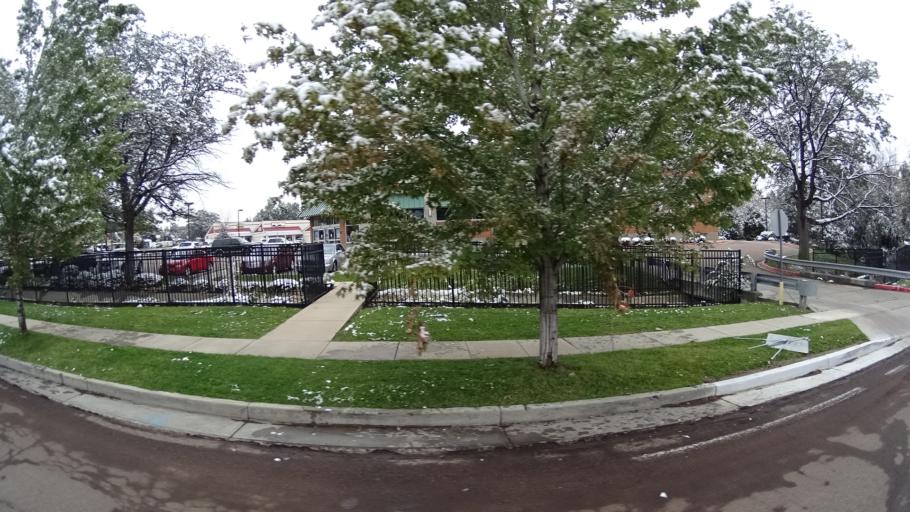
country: US
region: Colorado
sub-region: El Paso County
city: Cimarron Hills
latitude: 38.9005
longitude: -104.7686
